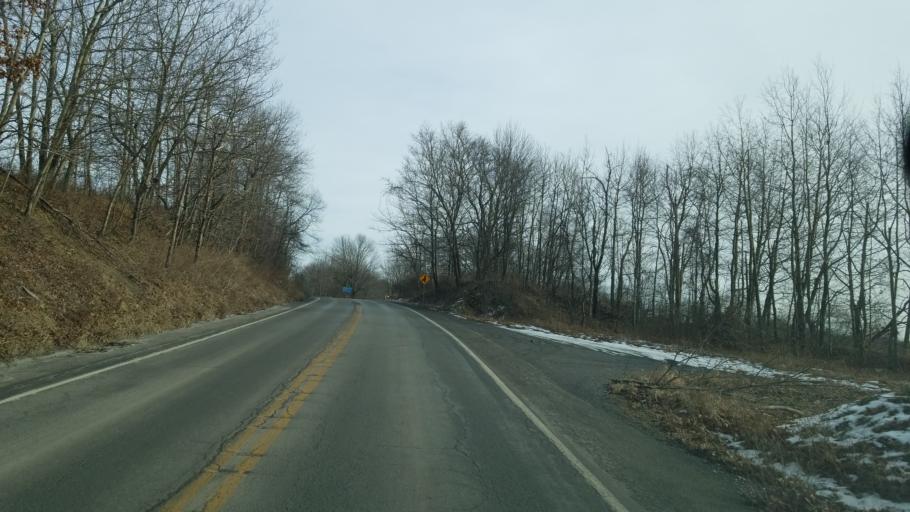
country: US
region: Pennsylvania
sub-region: Indiana County
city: Clymer
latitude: 40.7346
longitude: -78.9296
